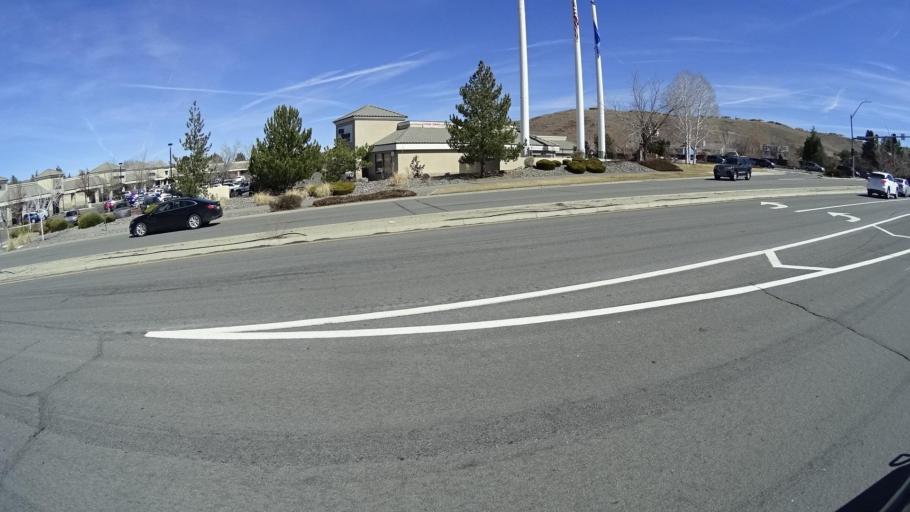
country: US
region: Nevada
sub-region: Washoe County
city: Sun Valley
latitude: 39.5863
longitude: -119.7160
